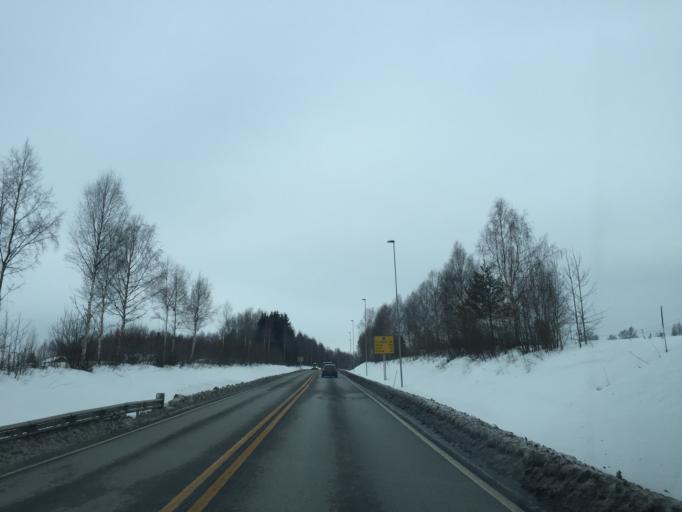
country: NO
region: Hedmark
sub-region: Loten
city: Loten
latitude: 60.7912
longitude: 11.2976
